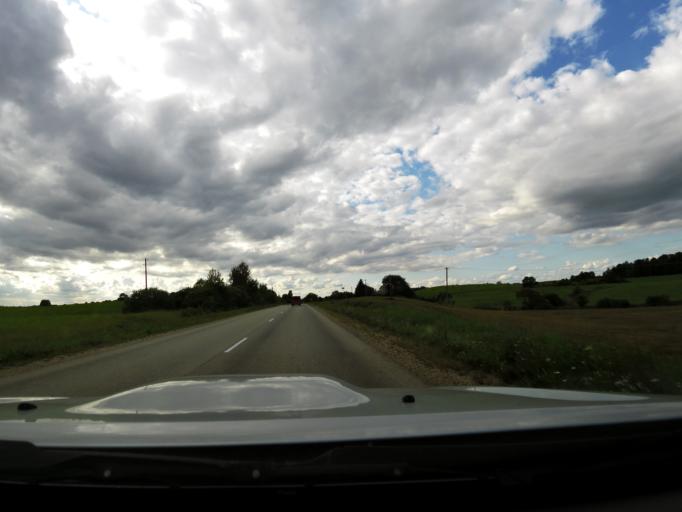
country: LV
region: Ilukste
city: Ilukste
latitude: 55.9755
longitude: 26.0174
